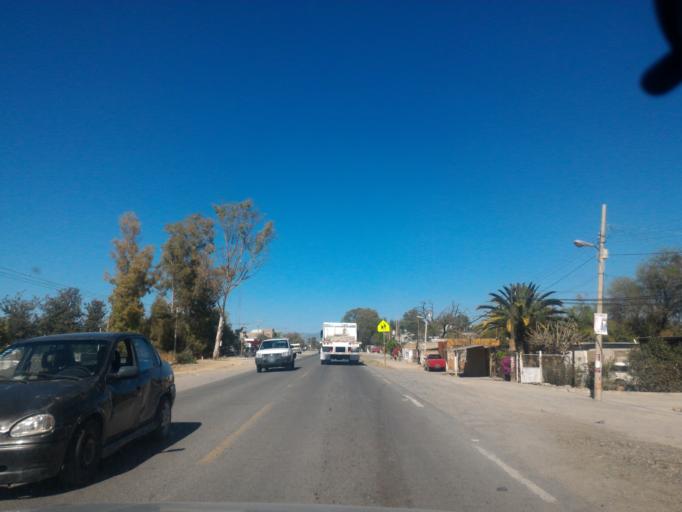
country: MX
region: Guanajuato
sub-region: Leon
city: Malagana (San Antonio del Monte)
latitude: 21.0388
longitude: -101.7693
